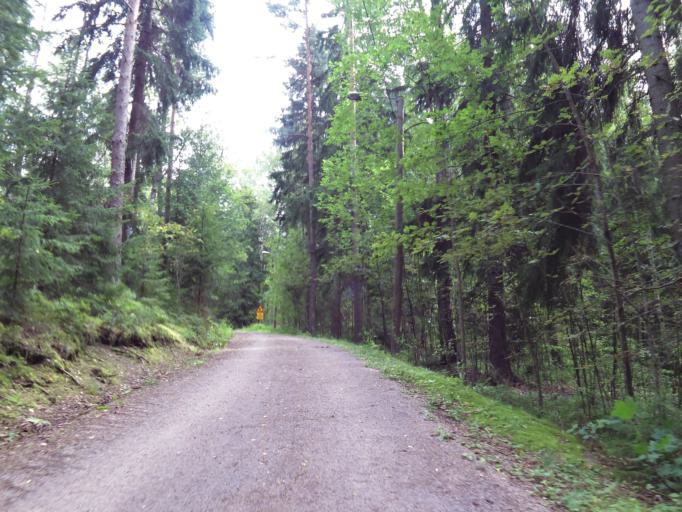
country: FI
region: Uusimaa
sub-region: Helsinki
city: Kauniainen
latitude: 60.1781
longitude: 24.7108
